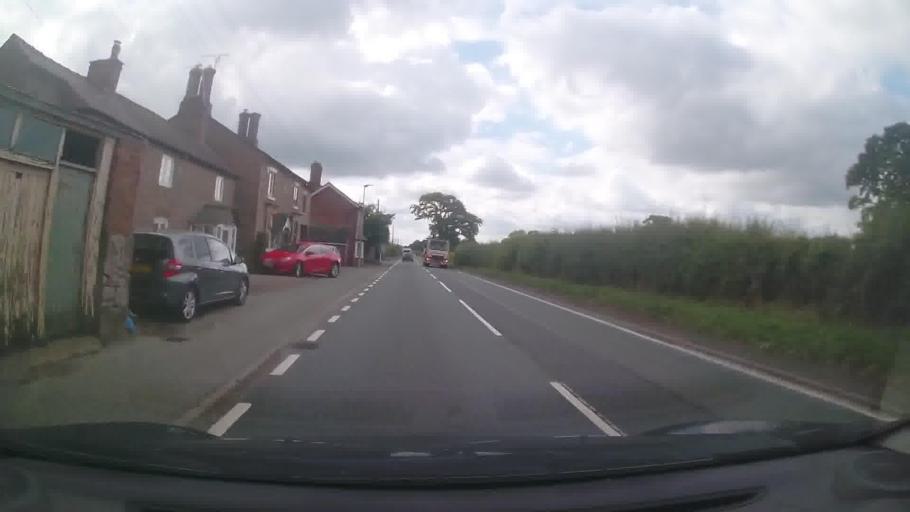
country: GB
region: England
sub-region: Shropshire
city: Pant
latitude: 52.7548
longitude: -3.0878
